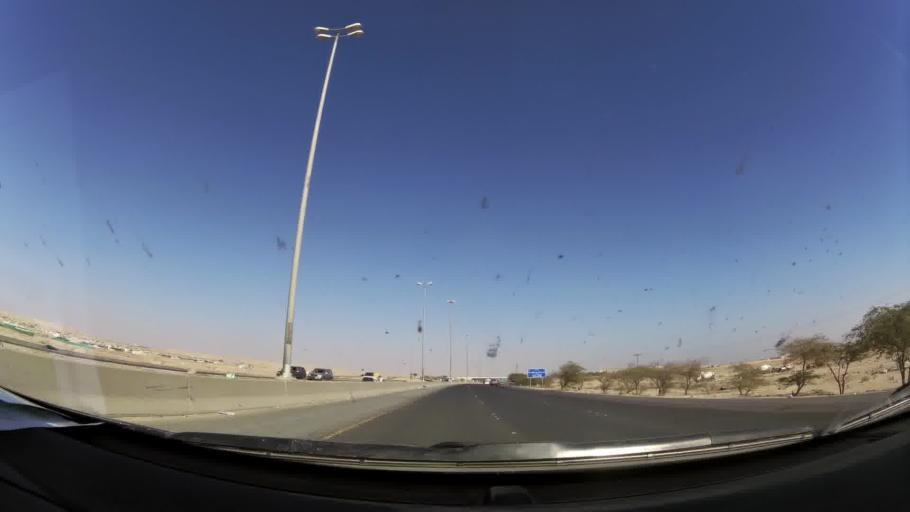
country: KW
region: Muhafazat al Jahra'
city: Al Jahra'
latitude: 29.3616
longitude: 47.6390
